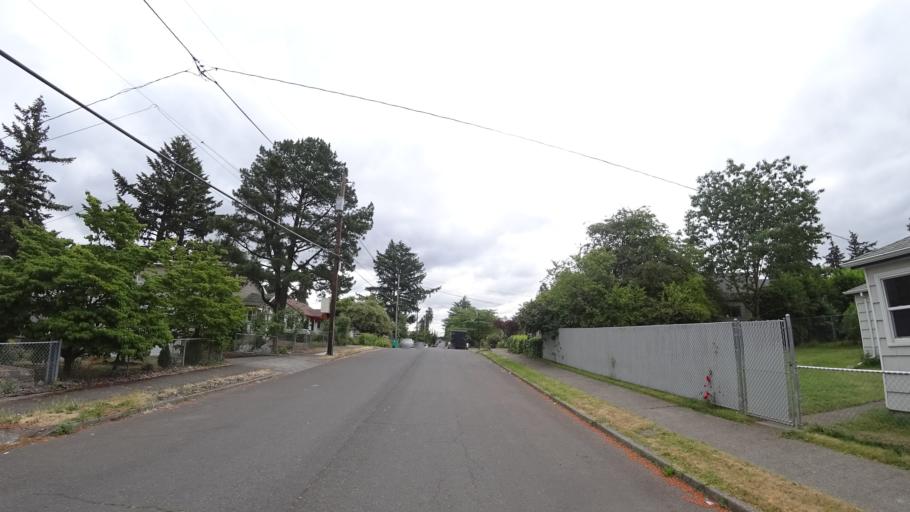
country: US
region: Oregon
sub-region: Multnomah County
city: Lents
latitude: 45.4782
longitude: -122.5841
